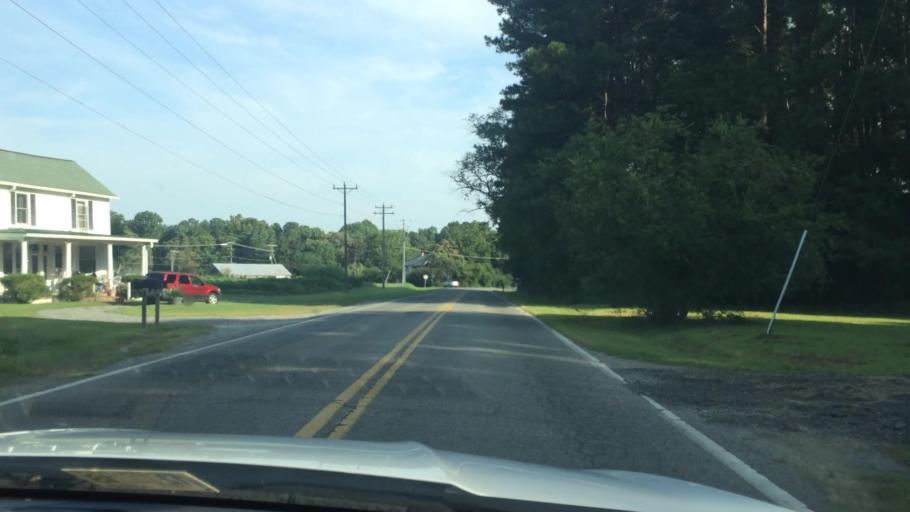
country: US
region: Virginia
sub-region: Middlesex County
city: Deltaville
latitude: 37.5774
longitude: -76.4561
